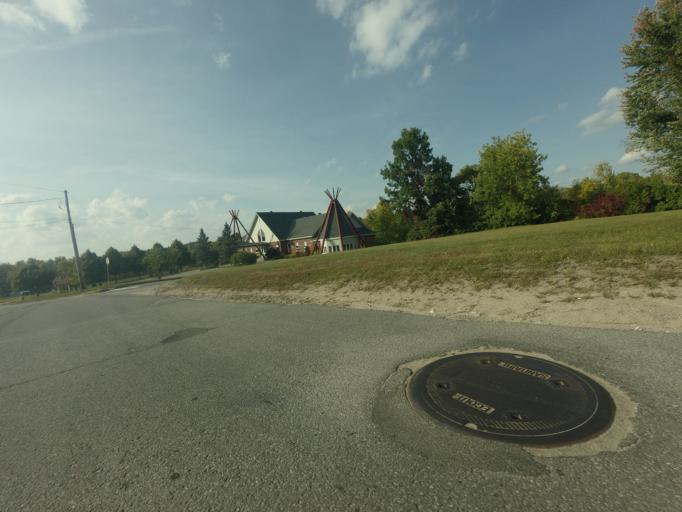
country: CA
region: Quebec
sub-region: Outaouais
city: Maniwaki
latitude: 46.3642
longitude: -75.9884
